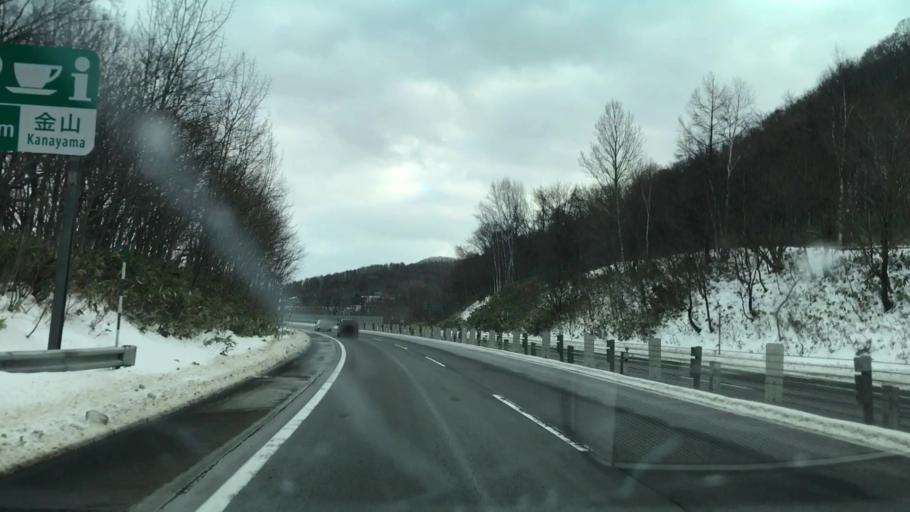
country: JP
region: Hokkaido
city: Sapporo
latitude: 43.1268
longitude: 141.1965
